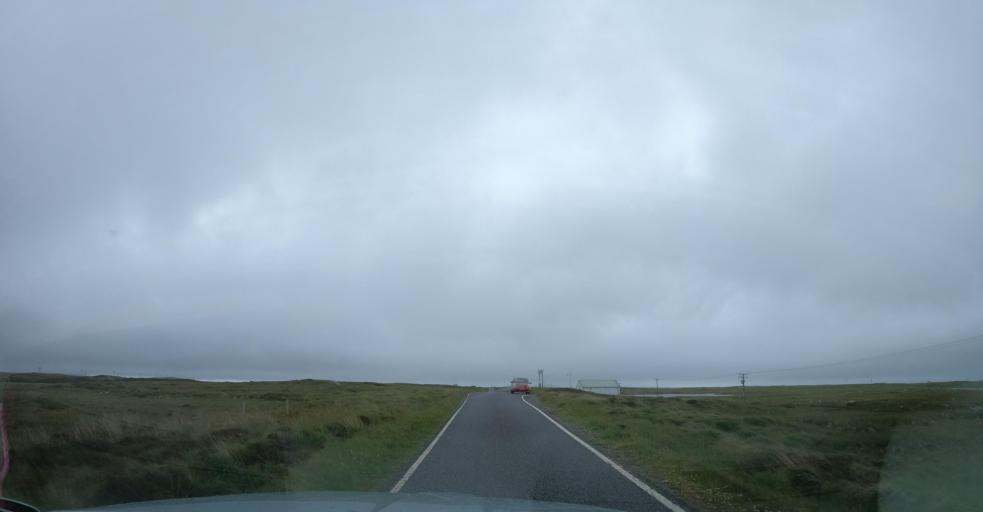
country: GB
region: Scotland
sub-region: Eilean Siar
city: Isle of North Uist
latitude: 57.5475
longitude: -7.3275
